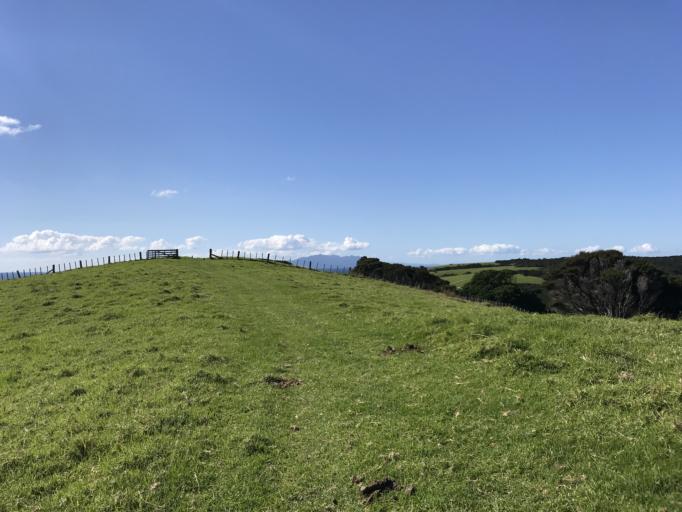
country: NZ
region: Auckland
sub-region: Auckland
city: Warkworth
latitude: -36.3751
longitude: 174.8325
